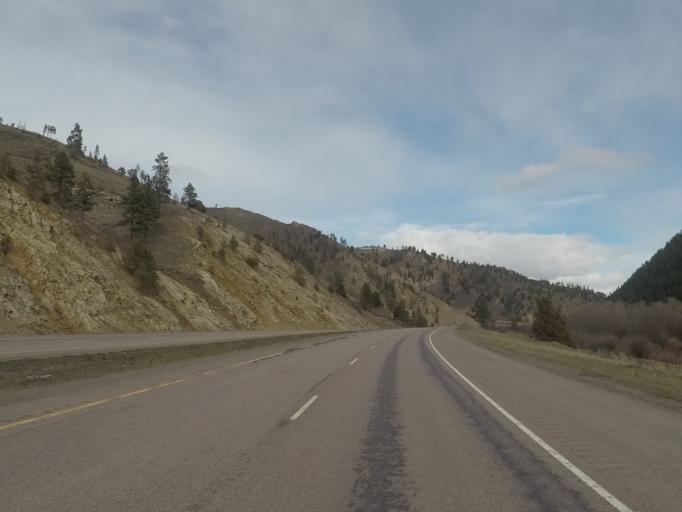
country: US
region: Montana
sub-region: Missoula County
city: Clinton
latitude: 46.7037
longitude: -113.4695
